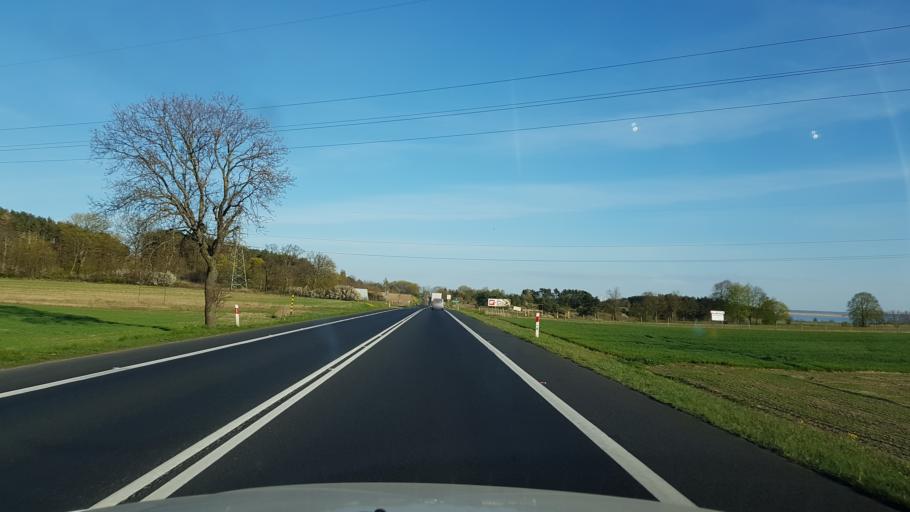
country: PL
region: West Pomeranian Voivodeship
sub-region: Powiat kamienski
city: Wolin
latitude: 53.8648
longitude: 14.5516
